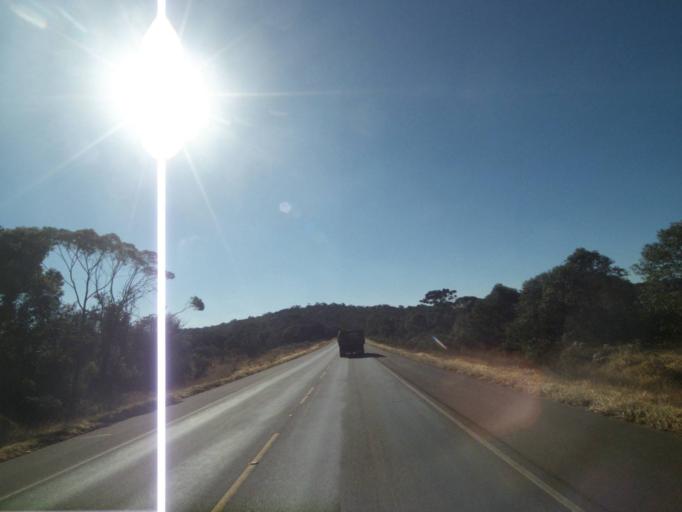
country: BR
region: Parana
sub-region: Tibagi
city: Tibagi
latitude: -24.6571
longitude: -50.4528
